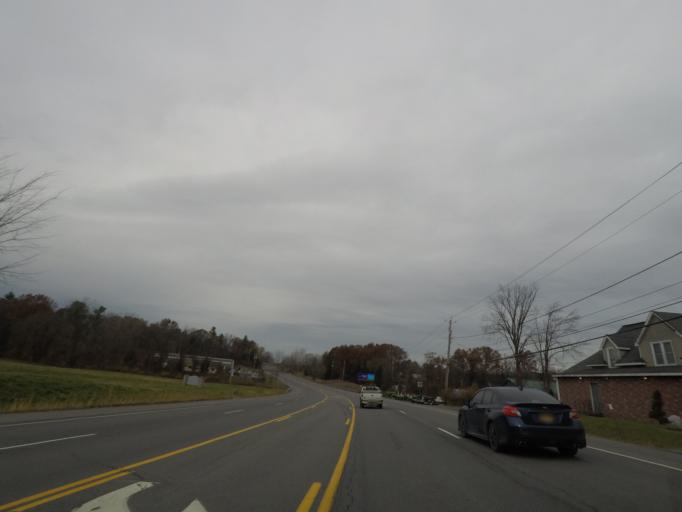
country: US
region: New York
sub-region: Saratoga County
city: Country Knolls
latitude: 42.9018
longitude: -73.7730
